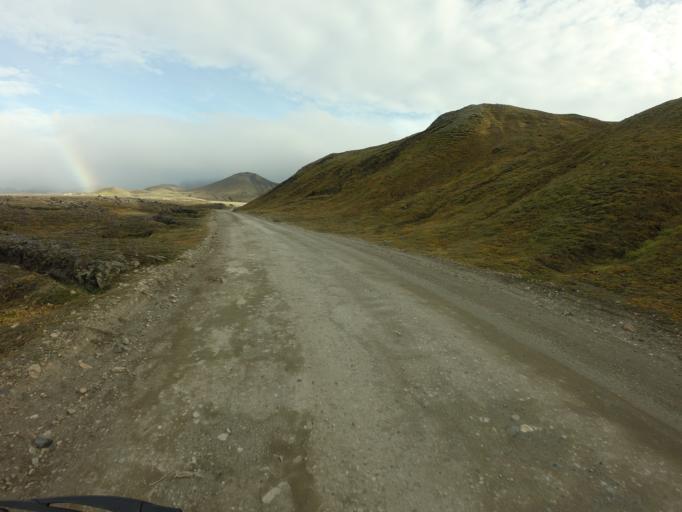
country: IS
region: South
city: Vestmannaeyjar
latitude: 64.0062
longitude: -19.0389
